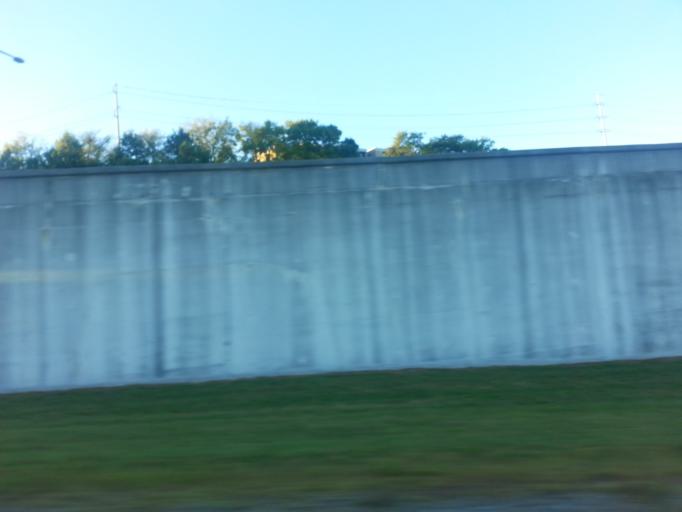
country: US
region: Tennessee
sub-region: Knox County
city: Knoxville
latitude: 35.9647
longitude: -83.9026
